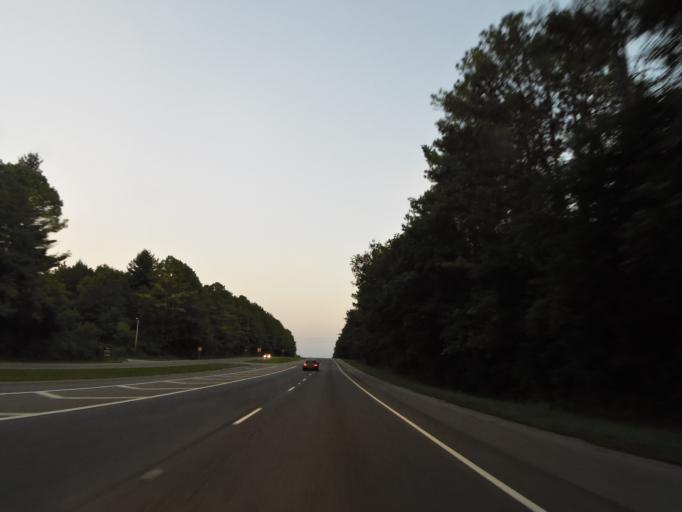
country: US
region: Tennessee
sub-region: Knox County
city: Farragut
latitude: 35.9635
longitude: -84.1725
